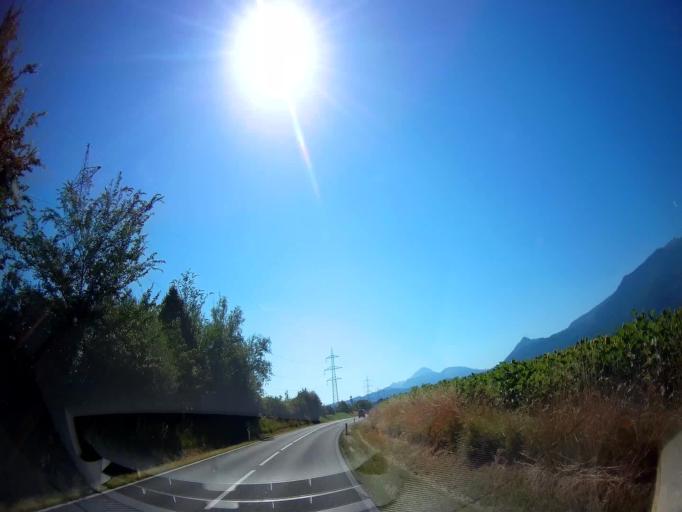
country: AT
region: Carinthia
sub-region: Politischer Bezirk Volkermarkt
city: Feistritz ob Bleiburg
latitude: 46.5757
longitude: 14.7403
